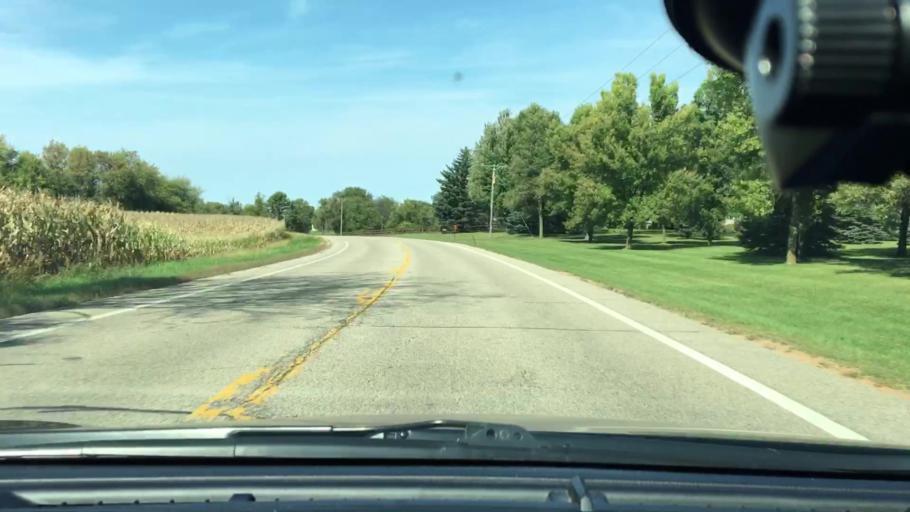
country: US
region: Minnesota
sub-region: Hennepin County
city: Corcoran
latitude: 45.0995
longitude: -93.5536
